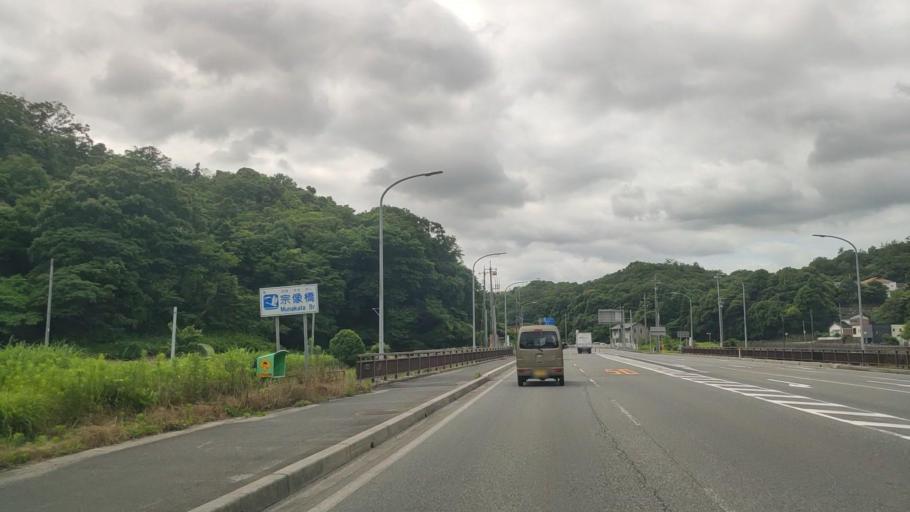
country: JP
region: Tottori
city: Yonago
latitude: 35.4162
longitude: 133.3528
